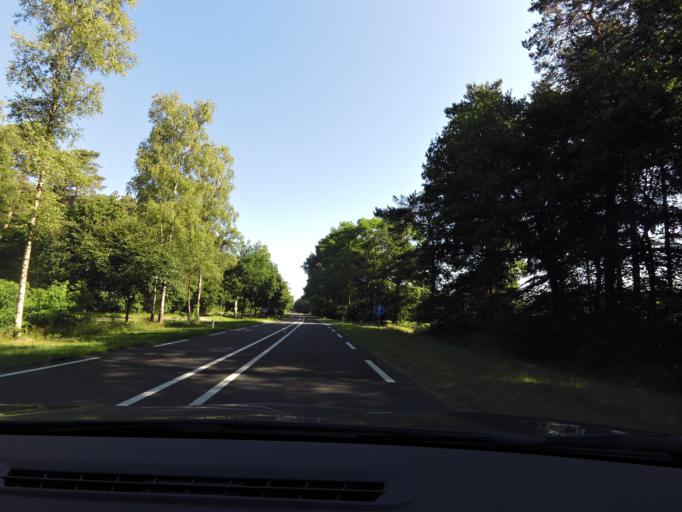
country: NL
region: Overijssel
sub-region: Gemeente Twenterand
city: Den Ham
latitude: 52.4785
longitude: 6.4277
